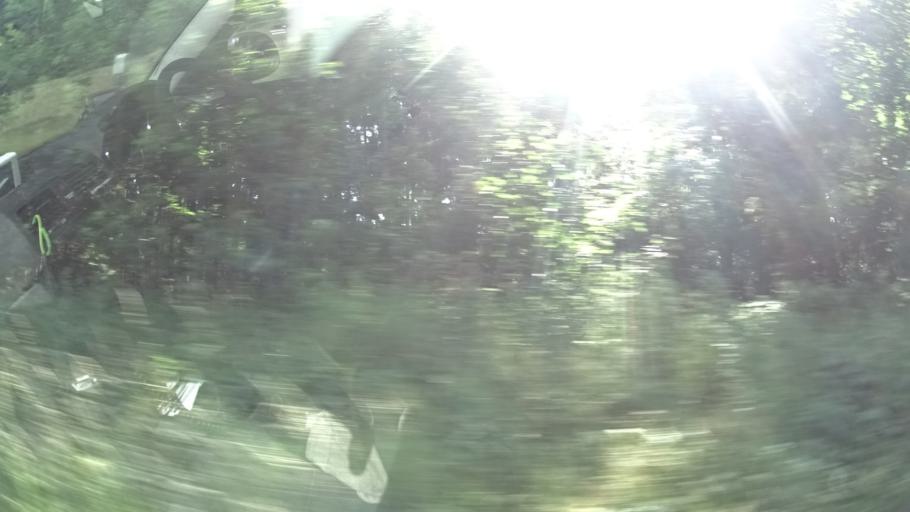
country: DE
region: Hesse
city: Rosenthal
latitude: 50.9328
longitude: 8.8393
